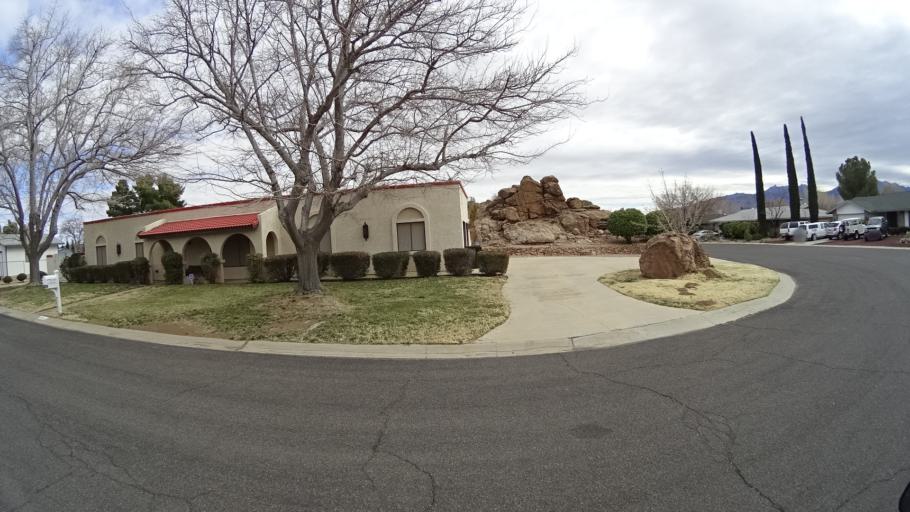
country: US
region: Arizona
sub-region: Mohave County
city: New Kingman-Butler
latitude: 35.2356
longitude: -114.0418
